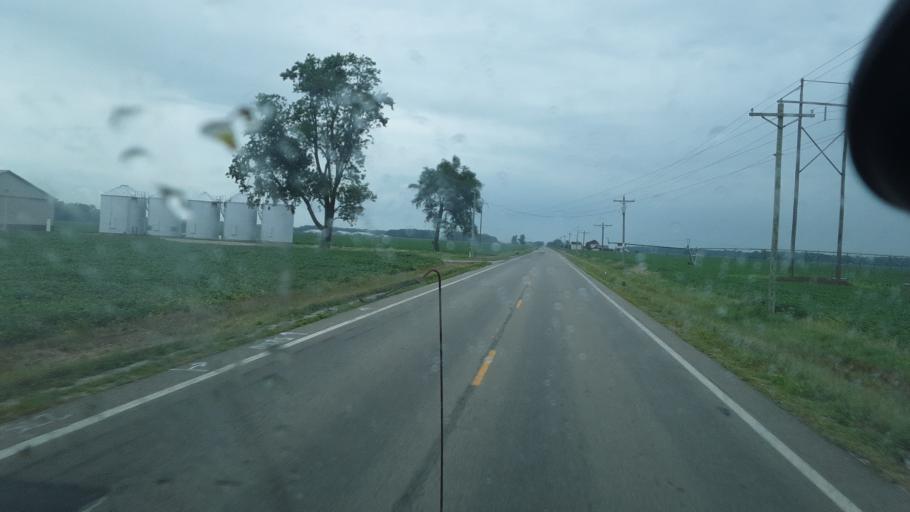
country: US
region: Ohio
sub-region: Defiance County
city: Hicksville
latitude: 41.2961
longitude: -84.6877
